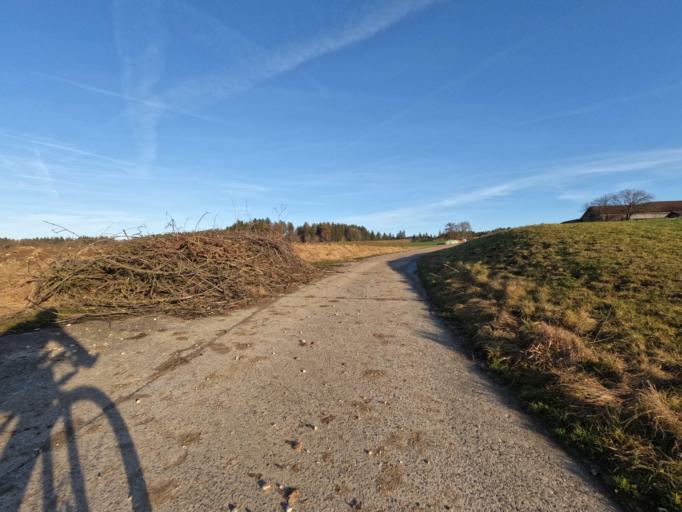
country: DE
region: Bavaria
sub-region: Upper Bavaria
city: Traunstein
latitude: 47.8984
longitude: 12.6298
